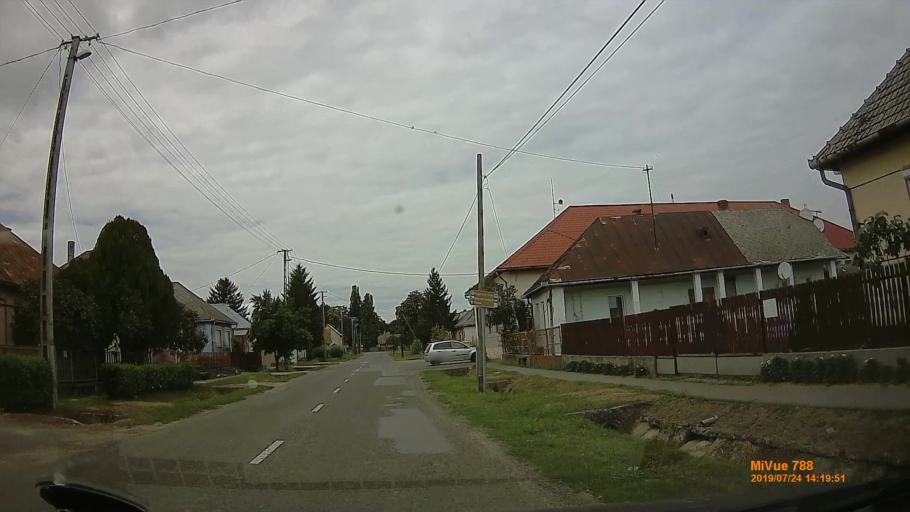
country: HU
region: Szabolcs-Szatmar-Bereg
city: Mandok
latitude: 48.3210
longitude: 22.2684
